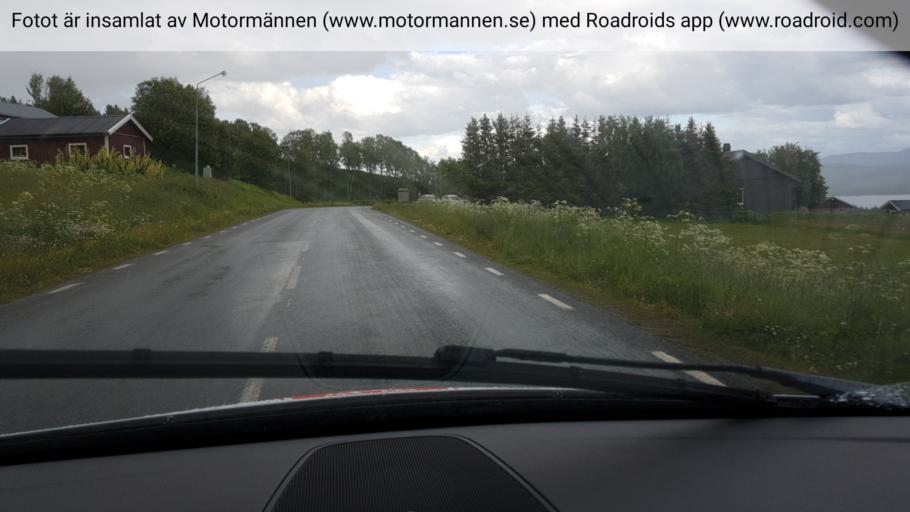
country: SE
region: Jaemtland
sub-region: Are Kommun
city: Are
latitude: 63.2166
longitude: 13.0505
